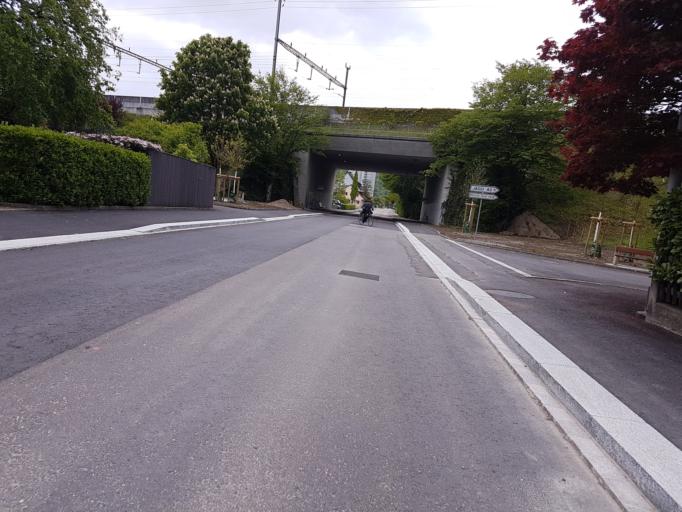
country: CH
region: Aargau
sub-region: Bezirk Brugg
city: Brugg
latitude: 47.4799
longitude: 8.2002
